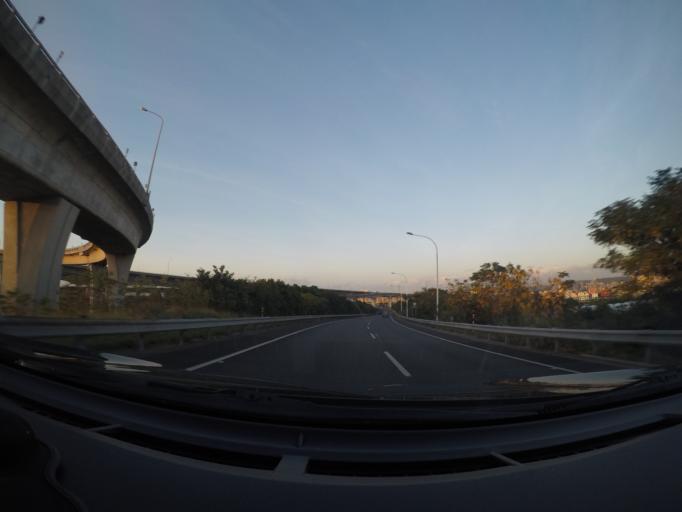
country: TW
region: Taiwan
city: Taoyuan City
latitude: 25.0186
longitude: 121.2763
